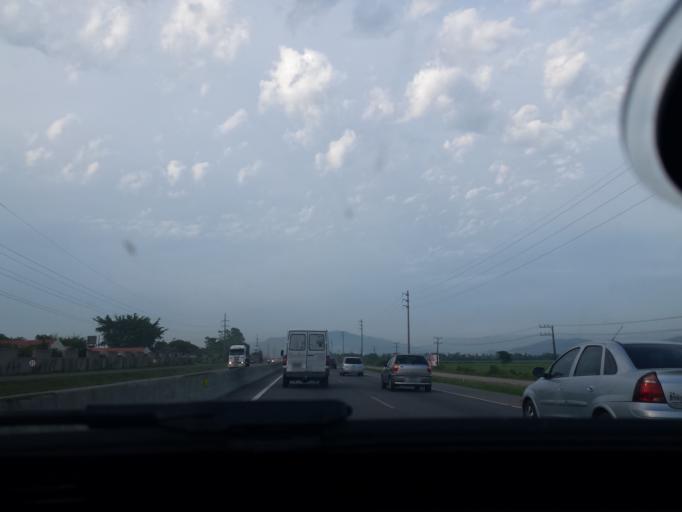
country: BR
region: Santa Catarina
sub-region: Tubarao
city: Tubarao
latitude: -28.4550
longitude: -48.9800
